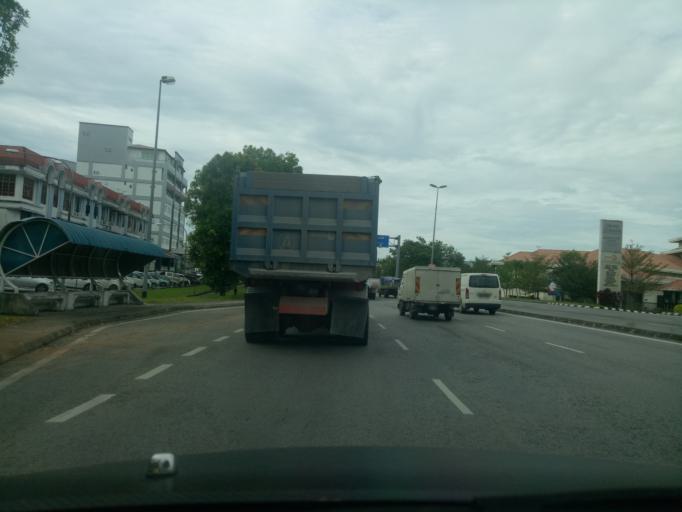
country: MY
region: Sarawak
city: Kuching
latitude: 1.5493
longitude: 110.3868
